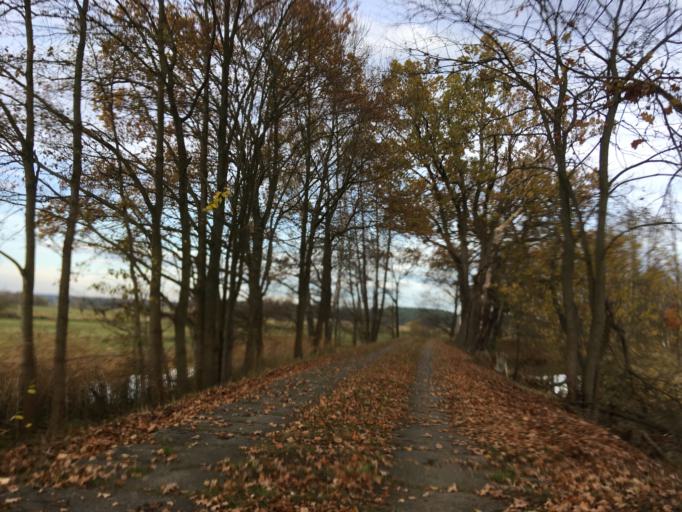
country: DE
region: Brandenburg
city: Schlepzig
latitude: 52.0246
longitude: 13.8548
